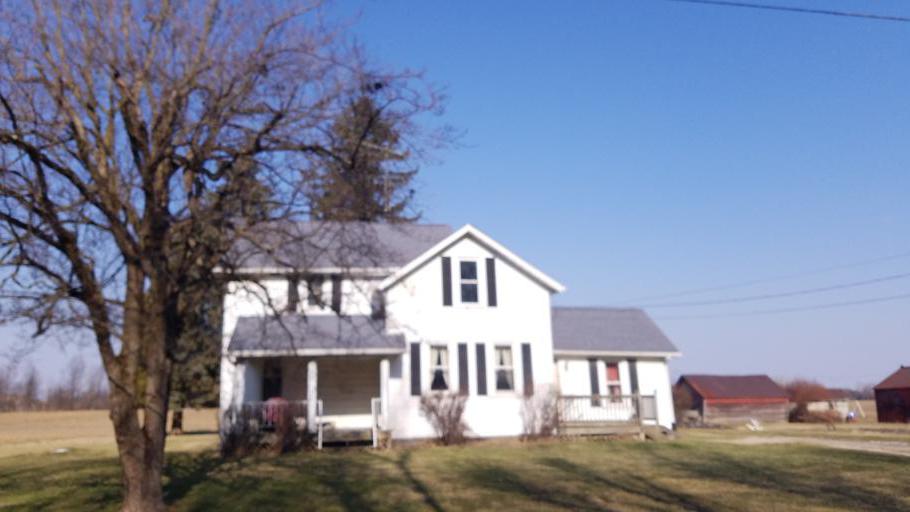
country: US
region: Ohio
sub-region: Richland County
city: Mansfield
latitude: 40.8287
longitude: -82.5468
